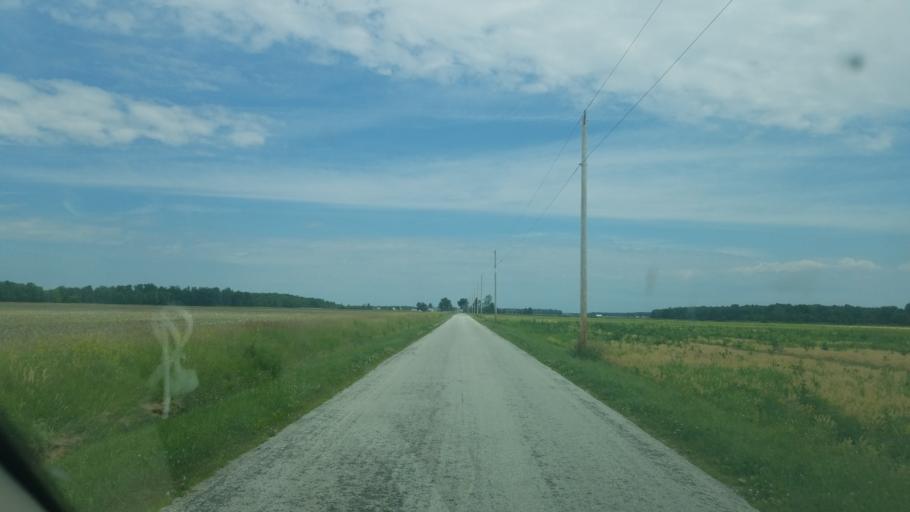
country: US
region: Ohio
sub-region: Wood County
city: North Baltimore
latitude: 41.2125
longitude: -83.5732
